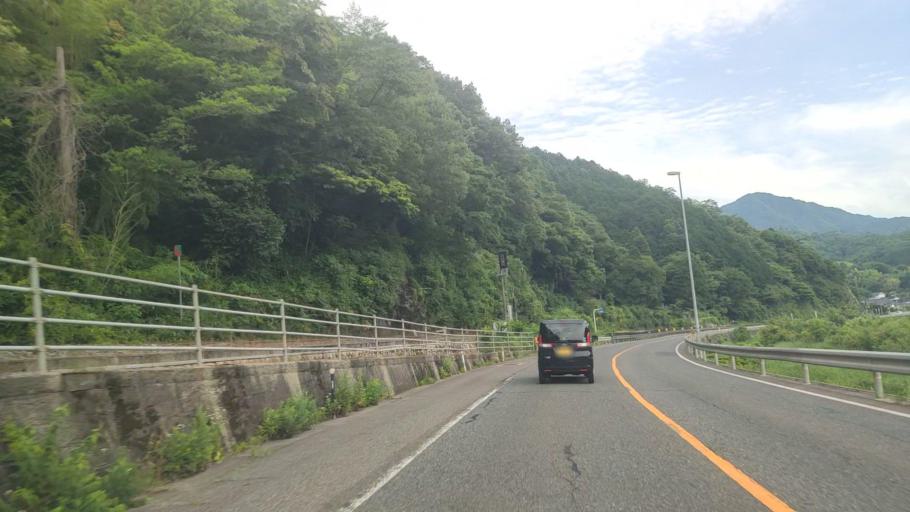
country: JP
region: Tottori
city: Tottori
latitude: 35.3489
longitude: 134.2053
